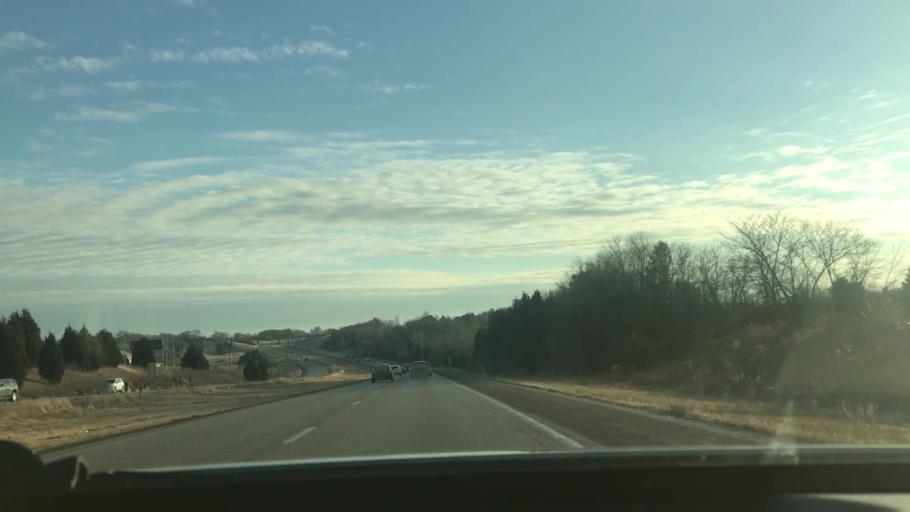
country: US
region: Missouri
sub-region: Jackson County
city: Blue Springs
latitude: 38.9929
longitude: -94.3577
